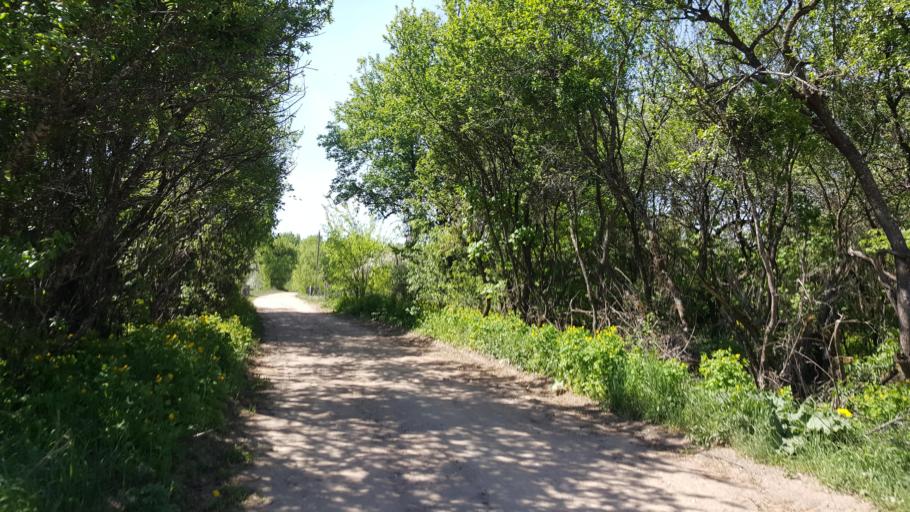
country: BY
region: Brest
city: Zhabinka
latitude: 52.3850
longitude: 24.0238
